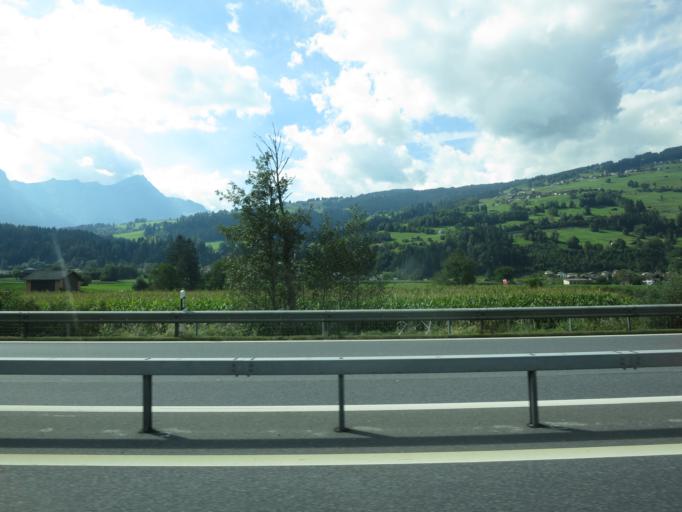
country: CH
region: Grisons
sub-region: Hinterrhein District
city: Cazis
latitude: 46.7183
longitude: 9.4421
